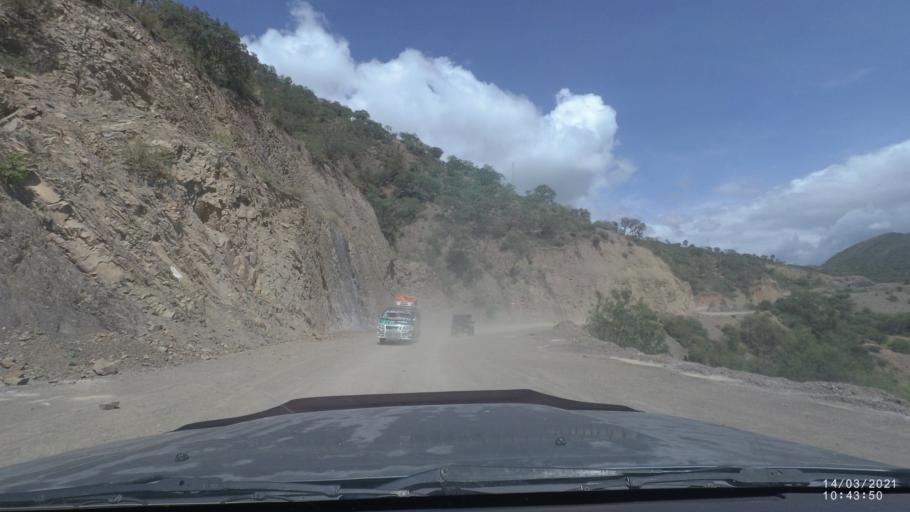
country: BO
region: Cochabamba
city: Tarata
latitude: -17.8780
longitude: -65.9273
